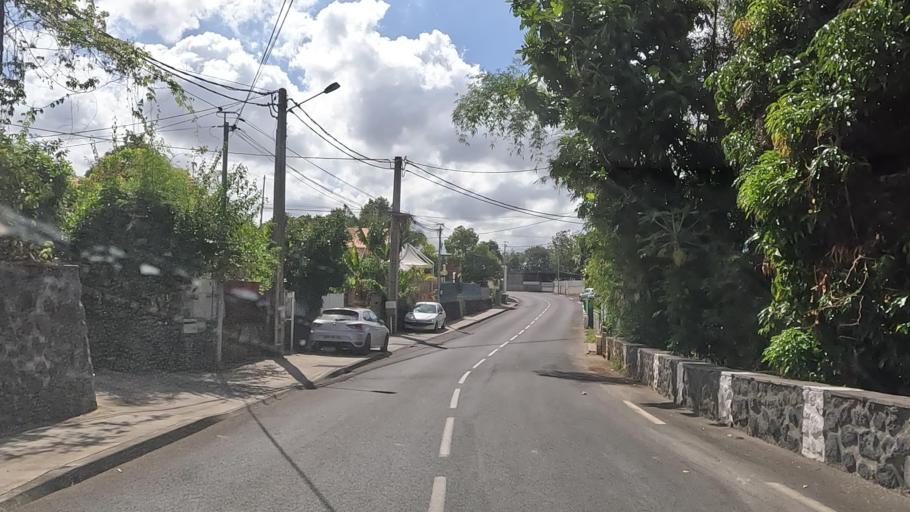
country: RE
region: Reunion
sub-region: Reunion
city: L'Entre-Deux
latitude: -21.2596
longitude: 55.4436
